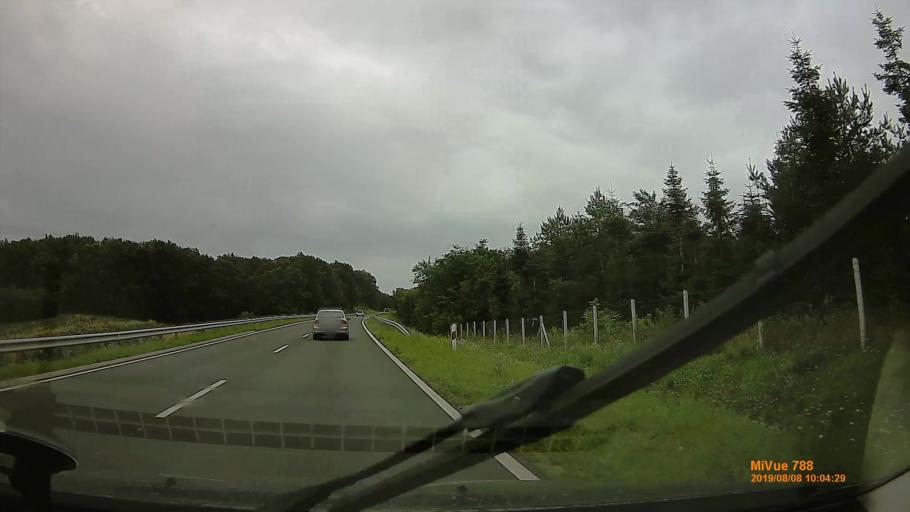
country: HU
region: Zala
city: Zalaegerszeg
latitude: 46.9136
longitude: 16.8593
